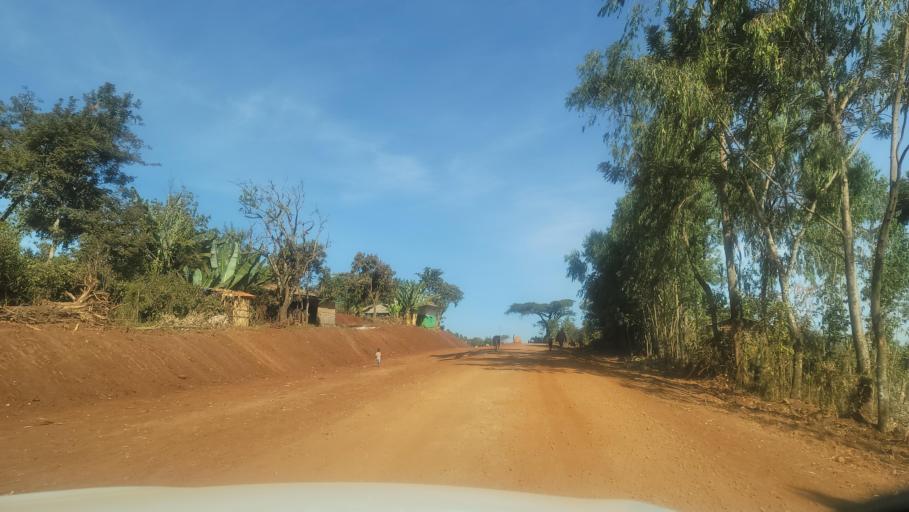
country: ET
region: Oromiya
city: Agaro
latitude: 7.8229
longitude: 36.5338
